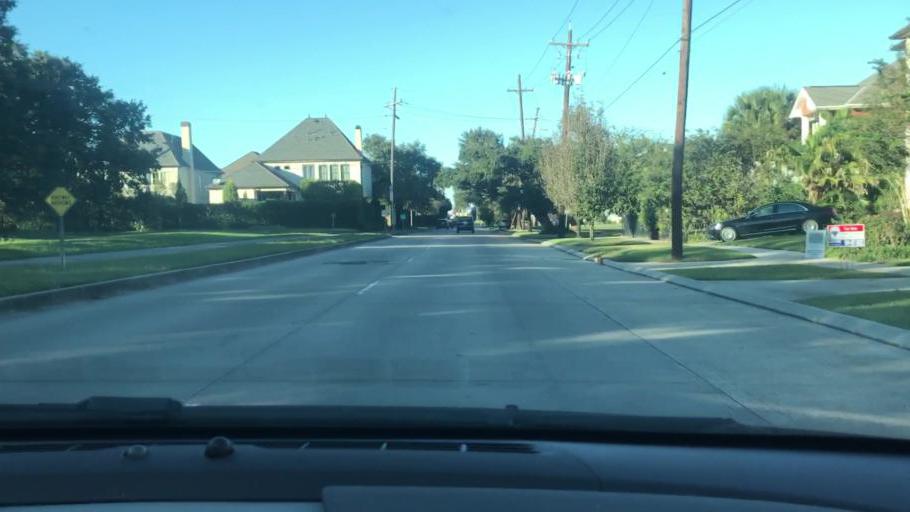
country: US
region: Louisiana
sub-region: Jefferson Parish
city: Metairie
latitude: 30.0173
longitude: -90.1137
